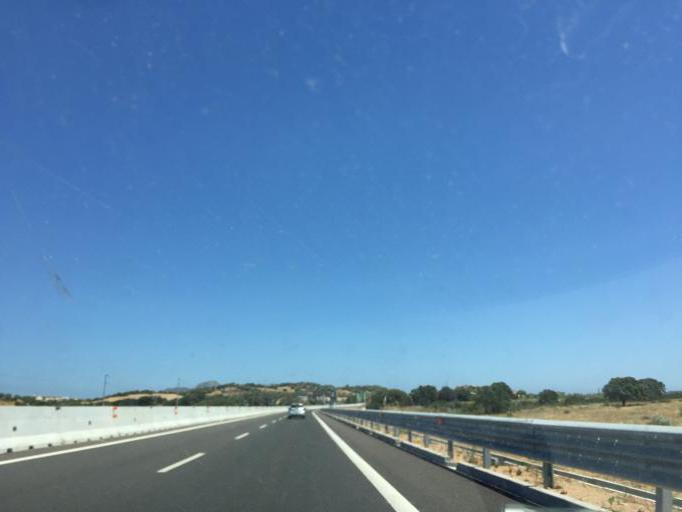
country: IT
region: Sardinia
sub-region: Provincia di Olbia-Tempio
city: Loiri Porto San Paolo
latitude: 40.8780
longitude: 9.4648
